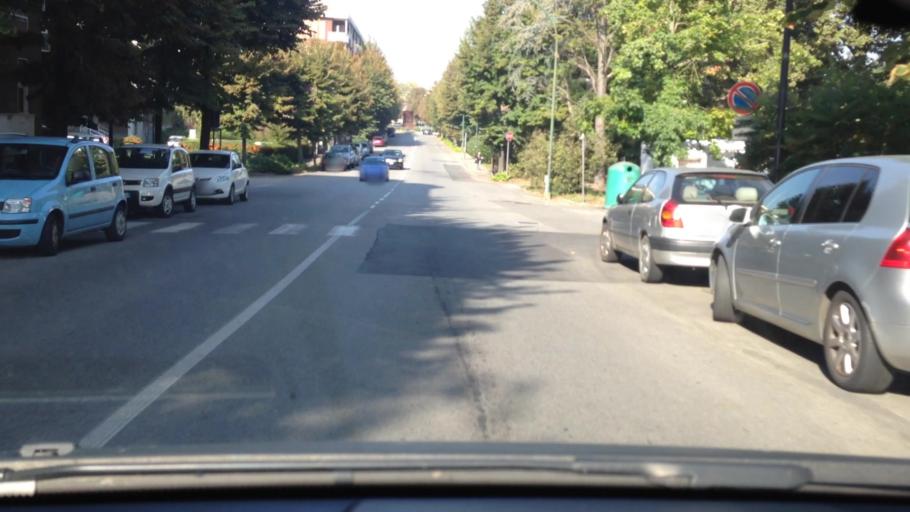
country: IT
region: Piedmont
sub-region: Provincia di Asti
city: Asti
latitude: 44.9061
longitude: 8.1940
